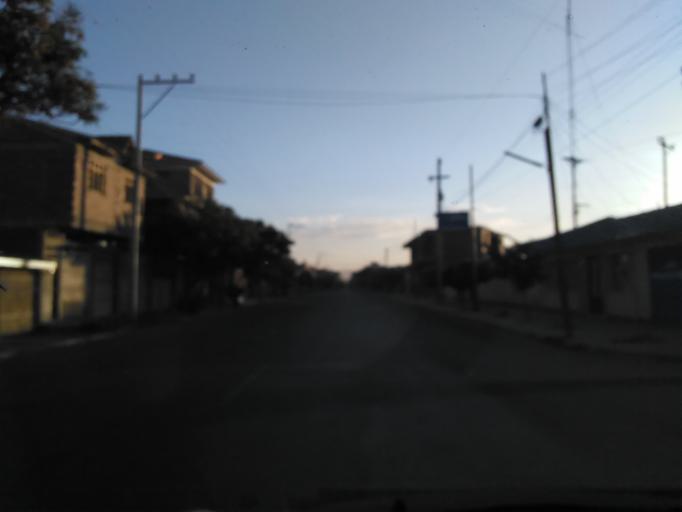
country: BO
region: Cochabamba
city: Punata
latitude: -17.5478
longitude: -65.8321
